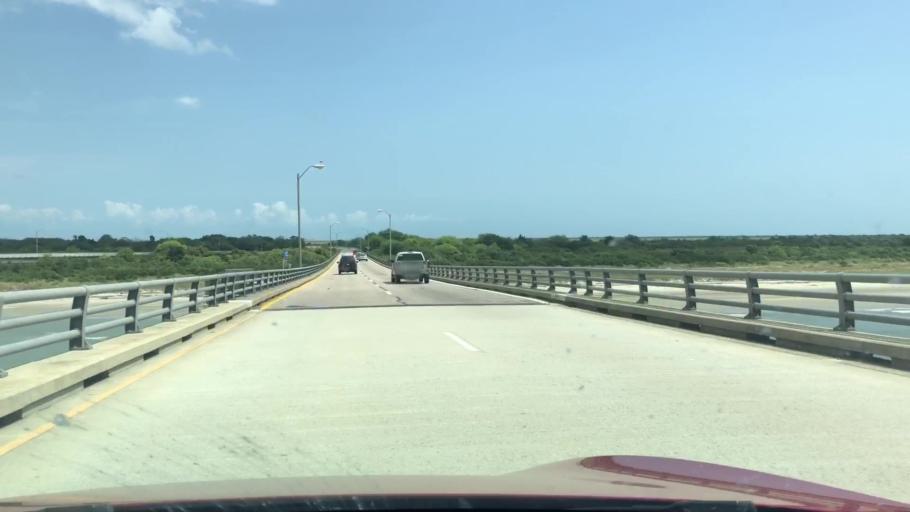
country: US
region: Virginia
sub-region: Northampton County
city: Cape Charles
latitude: 37.0907
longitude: -75.9814
